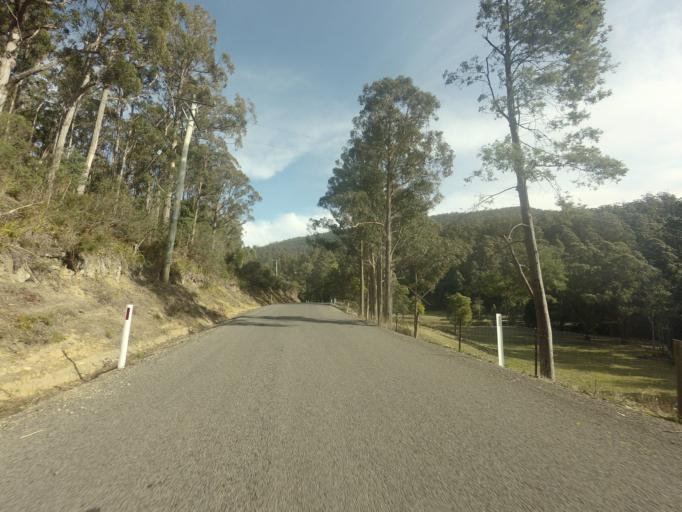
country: AU
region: Tasmania
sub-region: Huon Valley
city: Huonville
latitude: -43.0439
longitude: 147.1200
